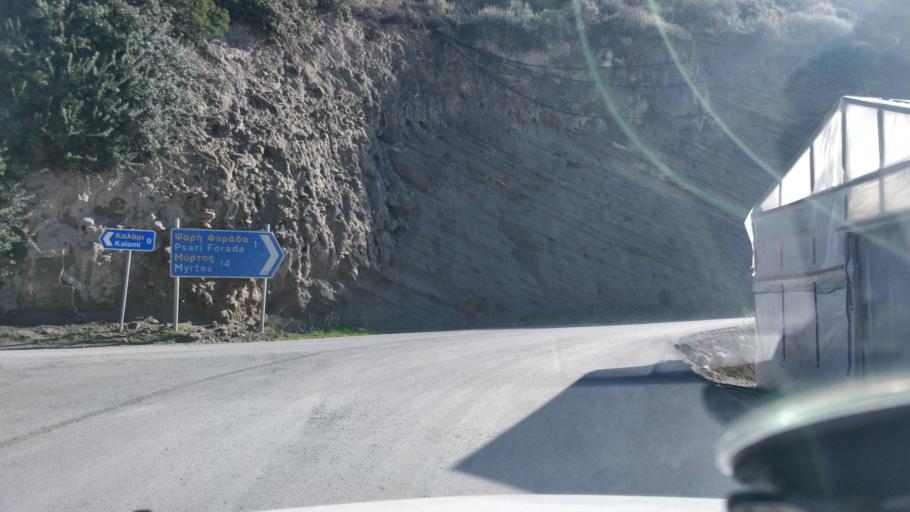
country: GR
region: Crete
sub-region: Nomos Lasithiou
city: Gra Liyia
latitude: 34.9900
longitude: 25.4846
